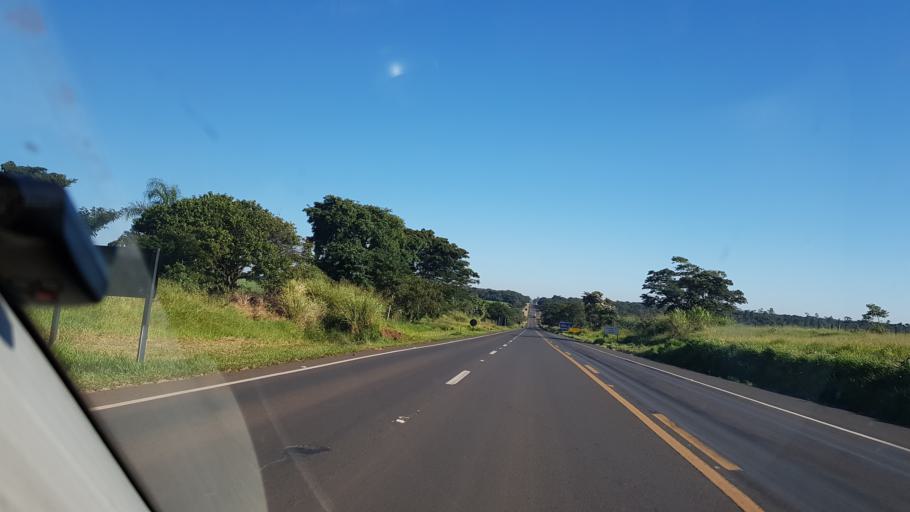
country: BR
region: Sao Paulo
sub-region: Assis
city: Assis
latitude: -22.5930
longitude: -50.4901
